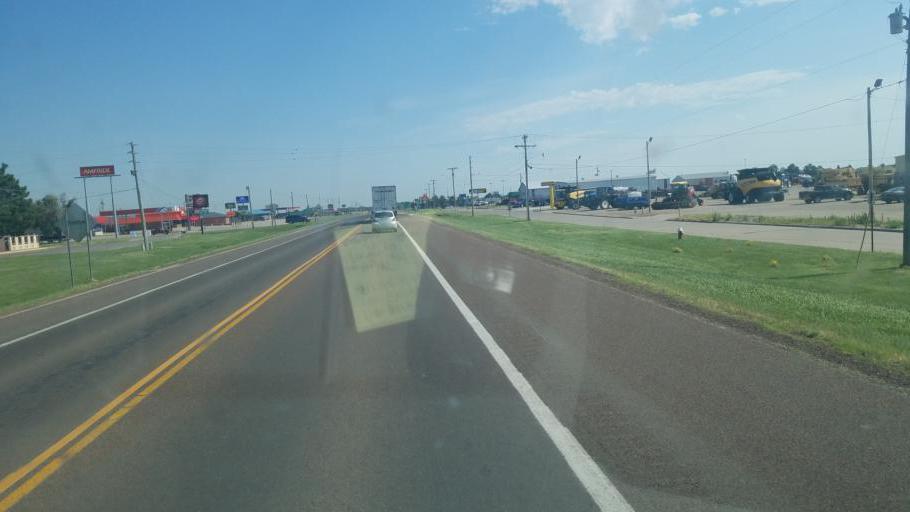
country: US
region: Kansas
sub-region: Ellsworth County
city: Ellsworth
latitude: 38.7360
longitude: -98.2155
